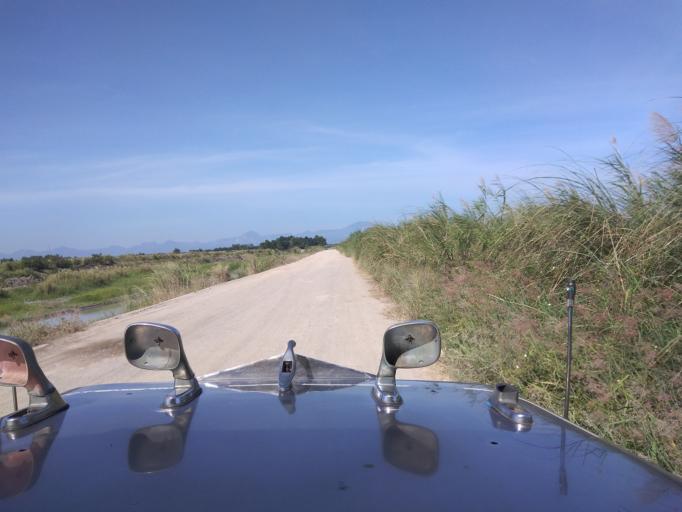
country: PH
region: Central Luzon
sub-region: Province of Pampanga
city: Minalin
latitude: 14.9908
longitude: 120.6767
